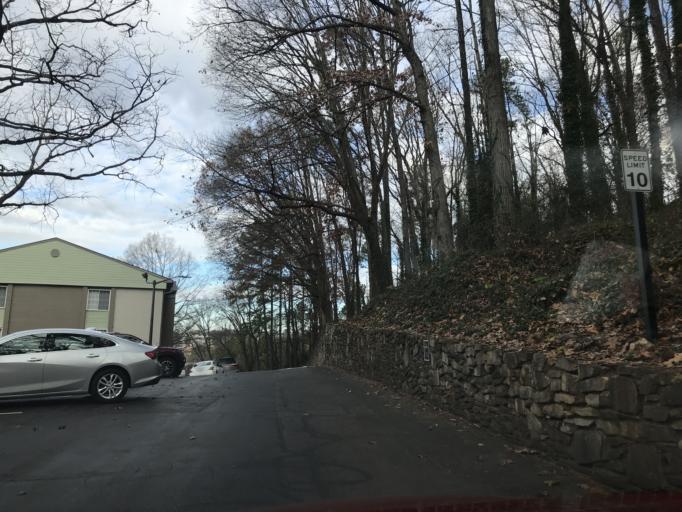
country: US
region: Georgia
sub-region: Fulton County
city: Sandy Springs
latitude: 33.9074
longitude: -84.3763
